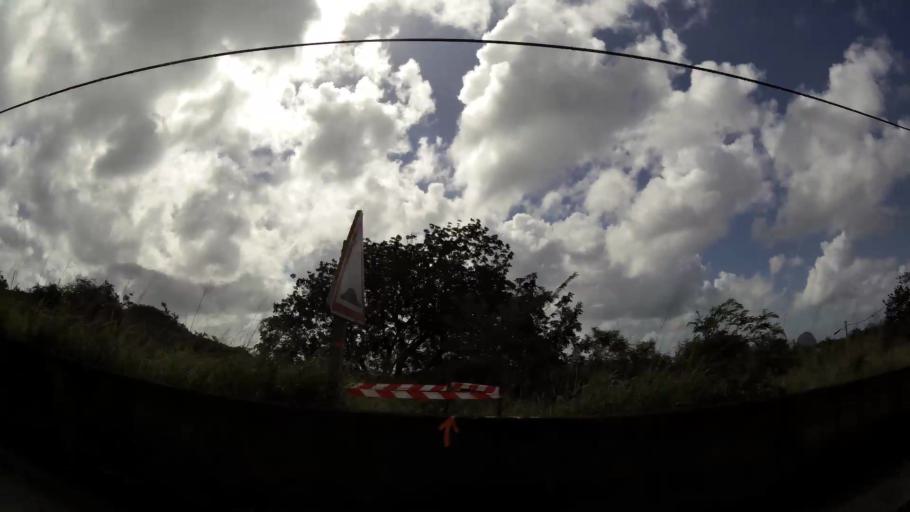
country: MQ
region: Martinique
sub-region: Martinique
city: Les Trois-Ilets
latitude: 14.4817
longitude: -61.0040
